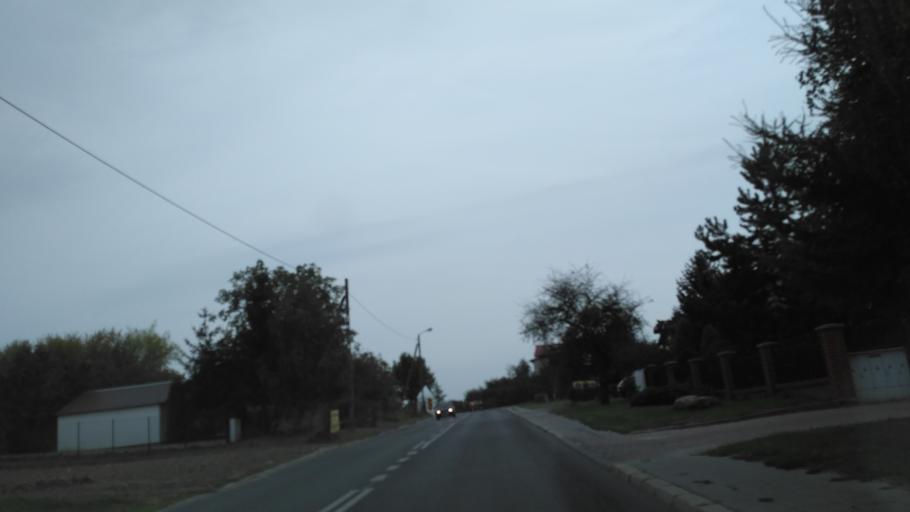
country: PL
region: Lublin Voivodeship
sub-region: Powiat lubelski
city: Lublin
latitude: 51.2139
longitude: 22.5923
